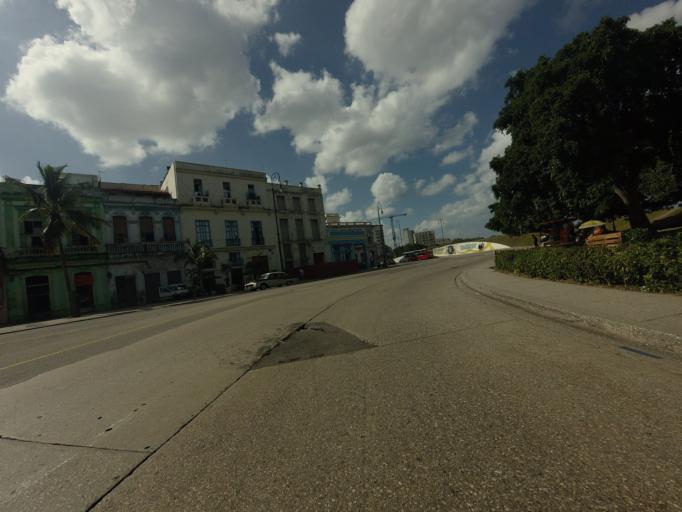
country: CU
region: La Habana
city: Centro Habana
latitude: 23.1438
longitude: -82.3546
